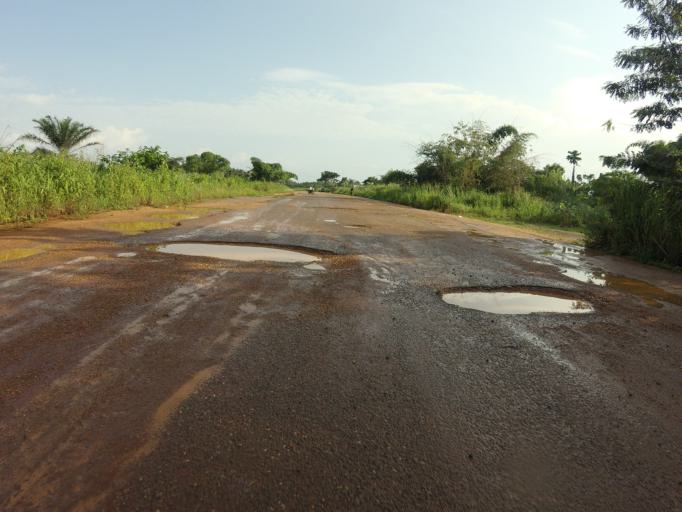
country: GH
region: Volta
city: Hohoe
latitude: 7.0733
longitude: 0.4363
